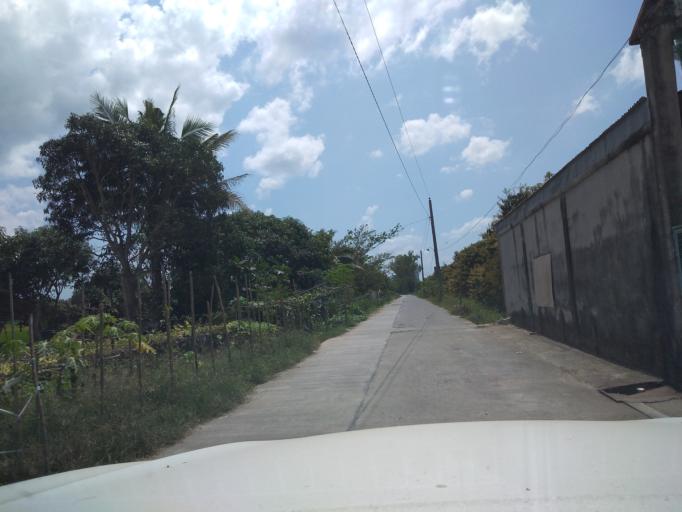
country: PH
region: Central Luzon
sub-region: Province of Pampanga
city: Lourdes
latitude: 15.0145
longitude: 120.8660
